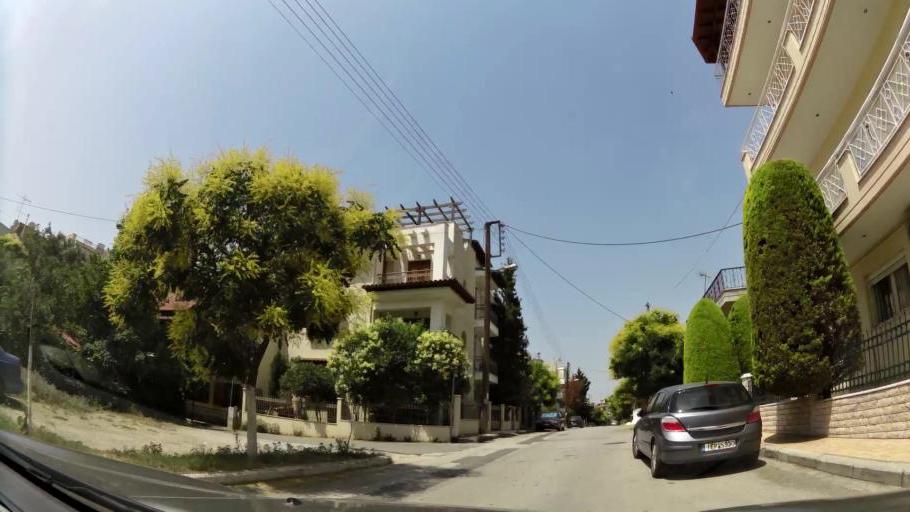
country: GR
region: Central Macedonia
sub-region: Nomos Thessalonikis
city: Evosmos
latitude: 40.6730
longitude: 22.8990
